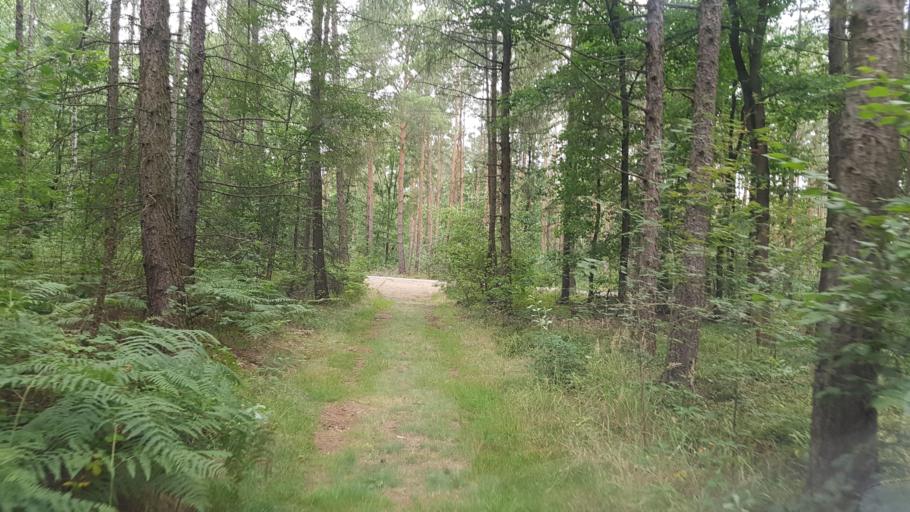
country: DE
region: Brandenburg
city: Schonborn
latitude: 51.6096
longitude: 13.5199
